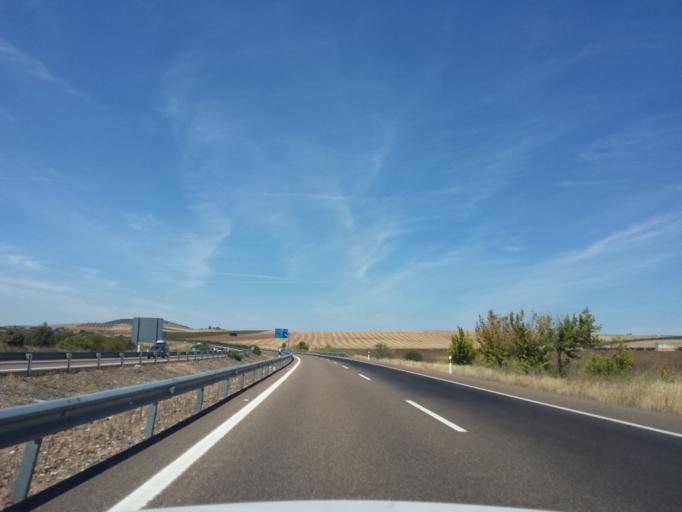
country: ES
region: Extremadura
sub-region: Provincia de Badajoz
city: Merida
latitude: 38.9464
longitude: -6.3152
